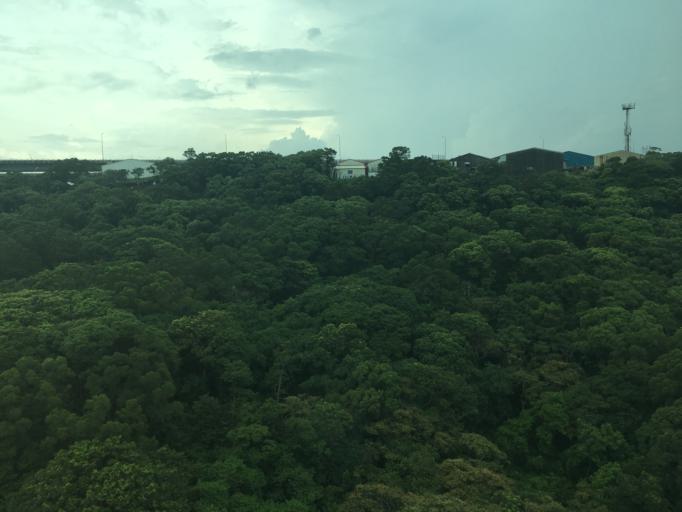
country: TW
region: Taiwan
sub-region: Taoyuan
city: Taoyuan
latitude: 25.0683
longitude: 121.3473
